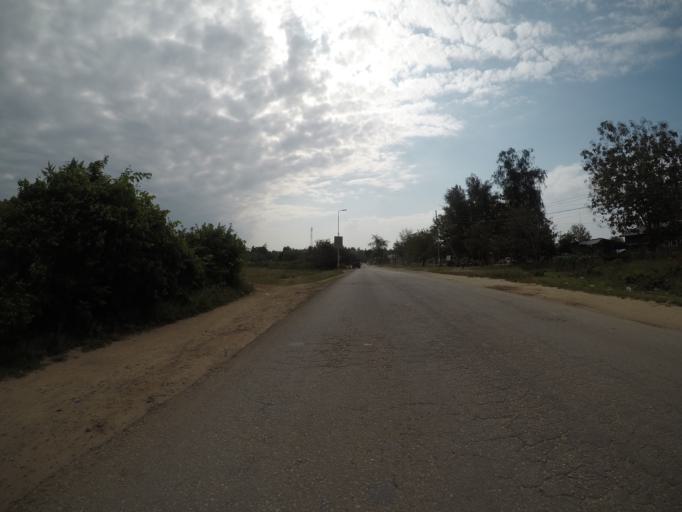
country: TZ
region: Zanzibar Central/South
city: Koani
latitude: -6.1962
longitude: 39.3053
